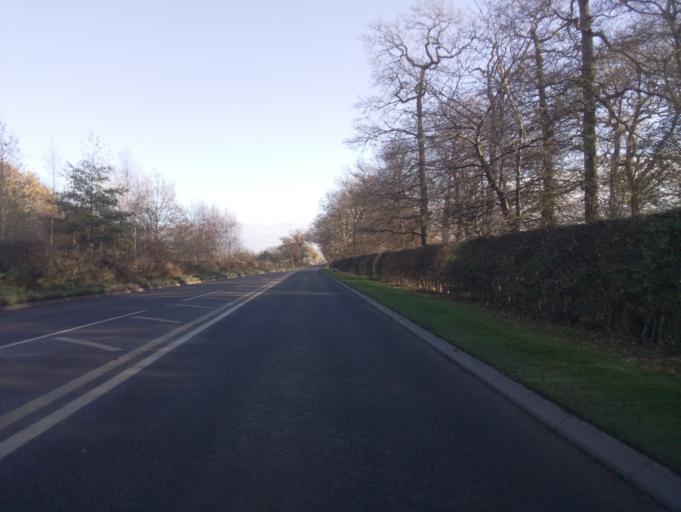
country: GB
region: England
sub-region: Staffordshire
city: Barton under Needwood
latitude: 52.8161
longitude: -1.7425
